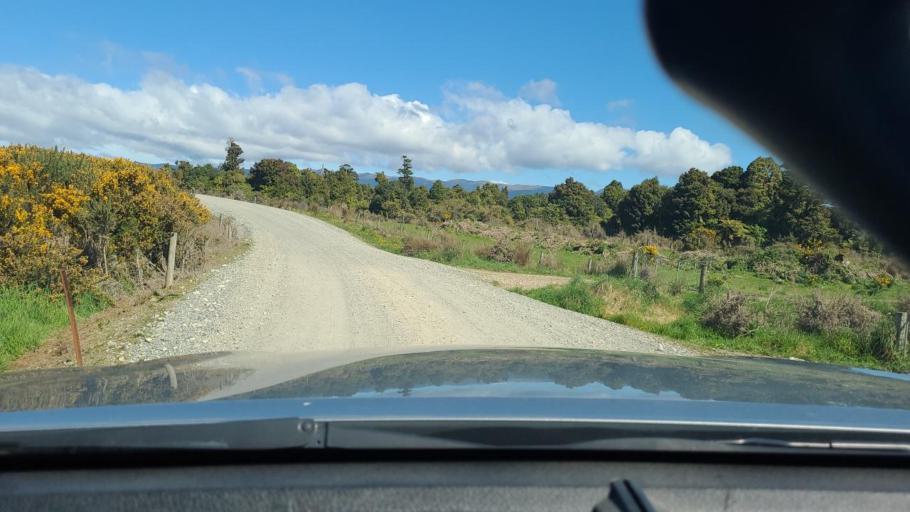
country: NZ
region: Southland
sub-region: Southland District
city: Riverton
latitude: -46.1417
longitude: 167.4799
